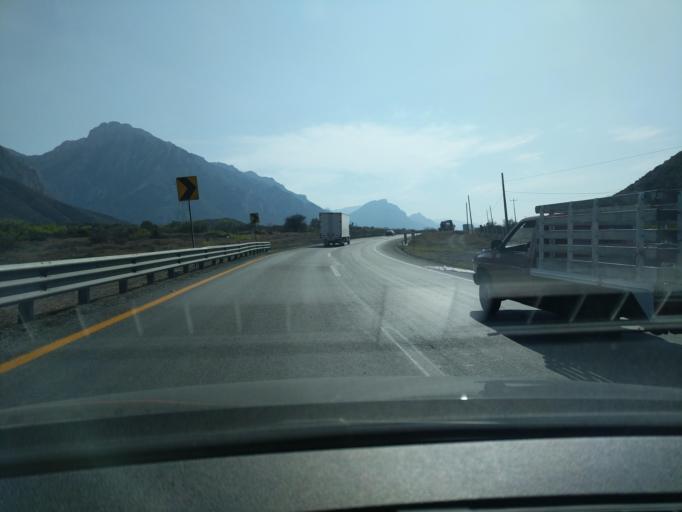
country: MX
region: Nuevo Leon
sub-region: Garcia
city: Las Torres de Guadalupe
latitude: 25.6834
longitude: -100.6607
